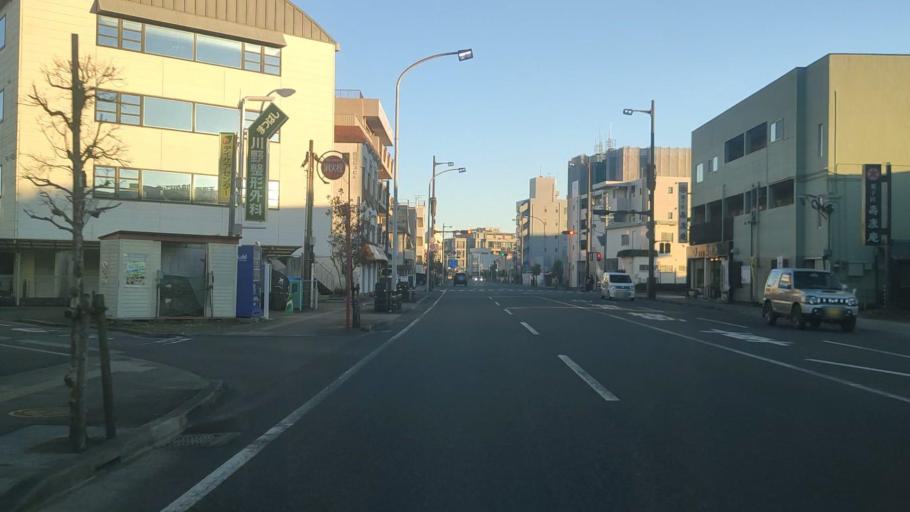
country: JP
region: Miyazaki
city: Miyazaki-shi
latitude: 31.9111
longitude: 131.4159
